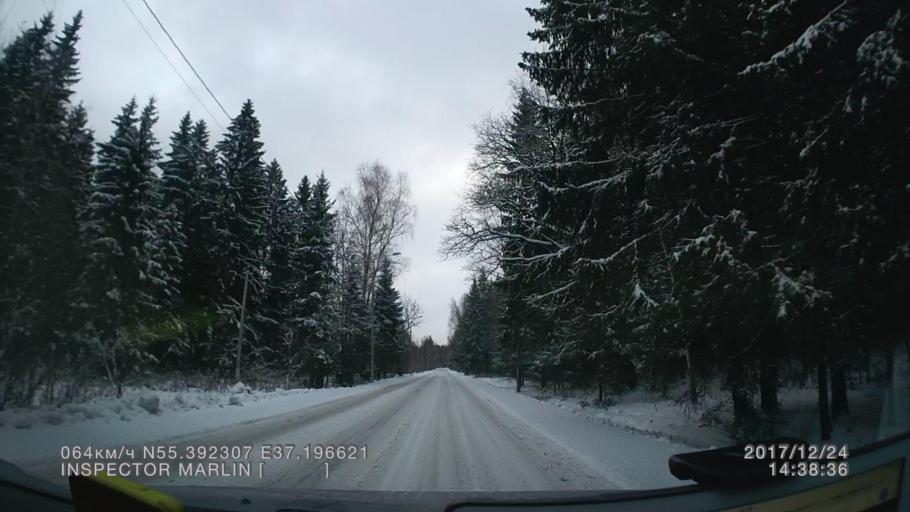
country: RU
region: Moskovskaya
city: Troitsk
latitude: 55.3922
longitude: 37.1967
